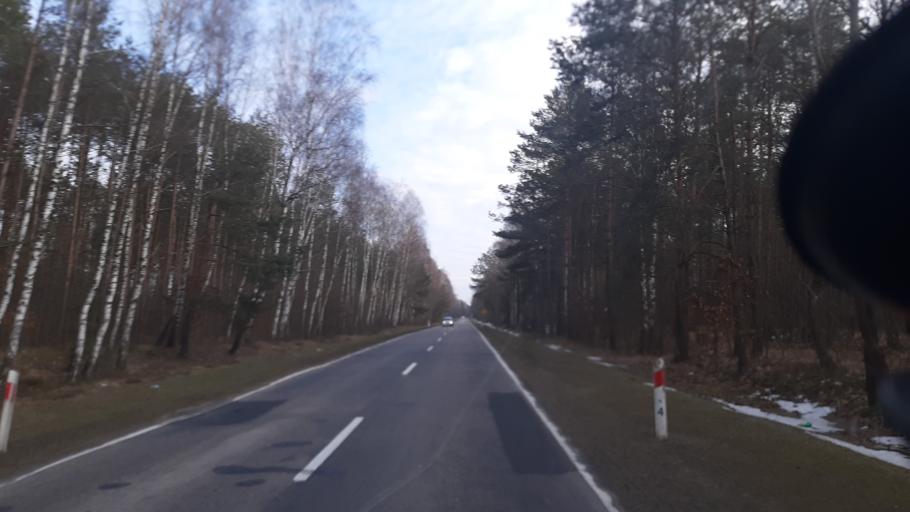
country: PL
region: Lublin Voivodeship
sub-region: Powiat lubartowski
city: Ostrow Lubelski
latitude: 51.4910
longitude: 22.8112
